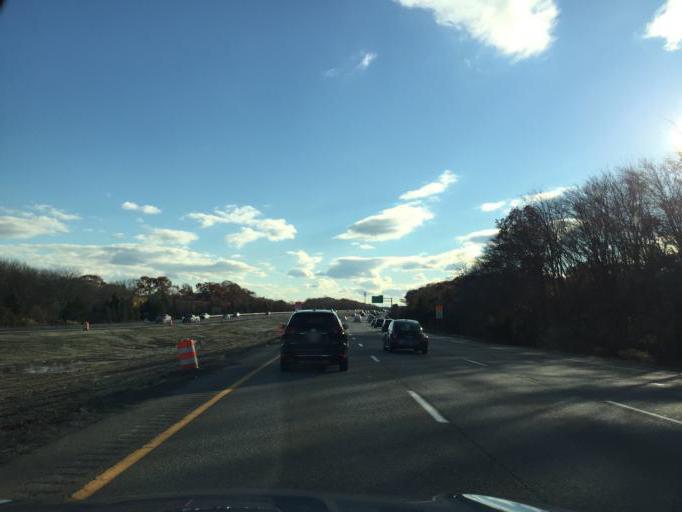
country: US
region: Massachusetts
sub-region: Bristol County
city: Attleboro
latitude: 41.9685
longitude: -71.2962
